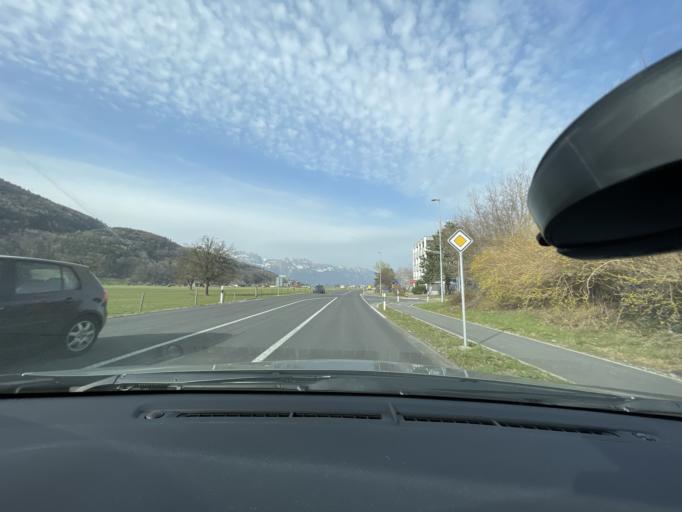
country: CH
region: Saint Gallen
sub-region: Wahlkreis Werdenberg
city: Sevelen
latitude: 47.1281
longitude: 9.4858
